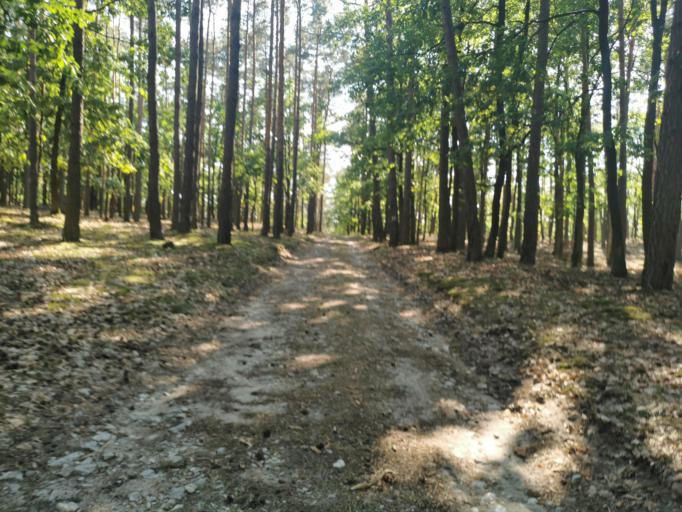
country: SK
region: Trnavsky
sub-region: Okres Senica
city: Senica
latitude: 48.6255
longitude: 17.2815
